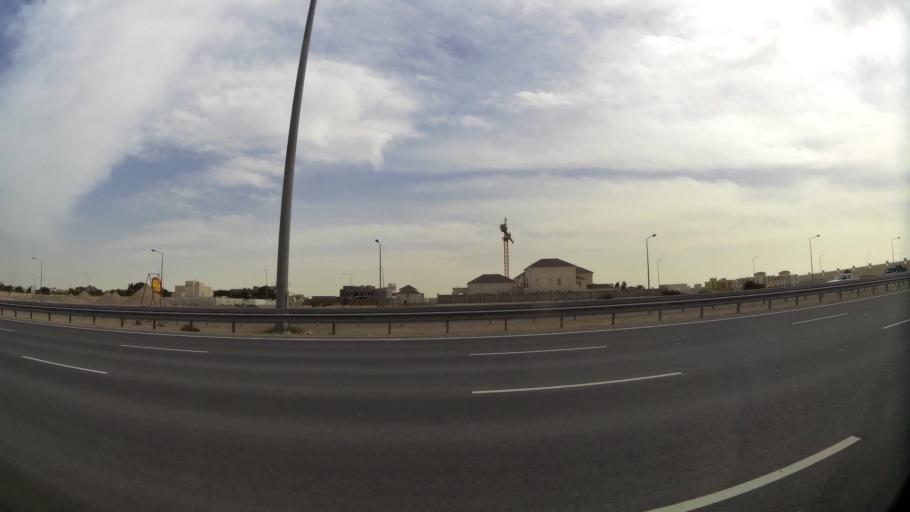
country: QA
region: Baladiyat ar Rayyan
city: Ar Rayyan
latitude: 25.3154
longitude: 51.3692
